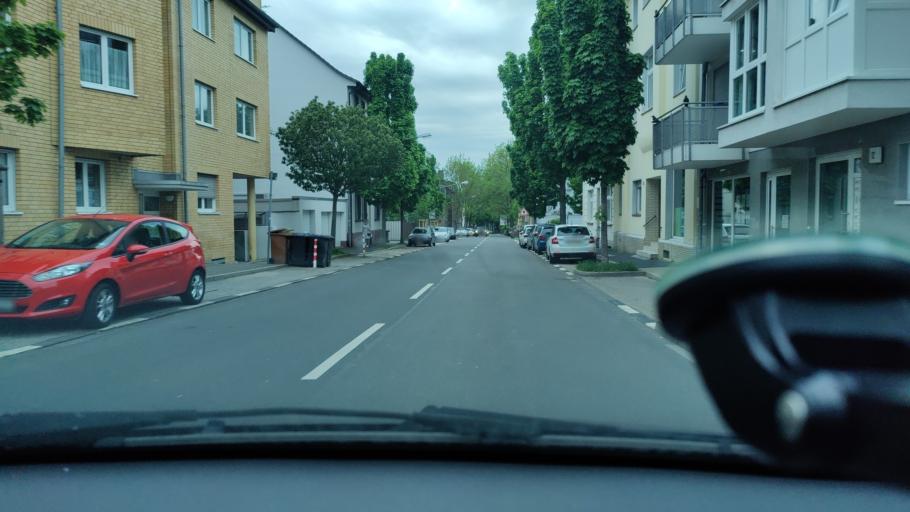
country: DE
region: North Rhine-Westphalia
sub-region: Regierungsbezirk Dusseldorf
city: Ratingen
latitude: 51.2996
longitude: 6.8458
